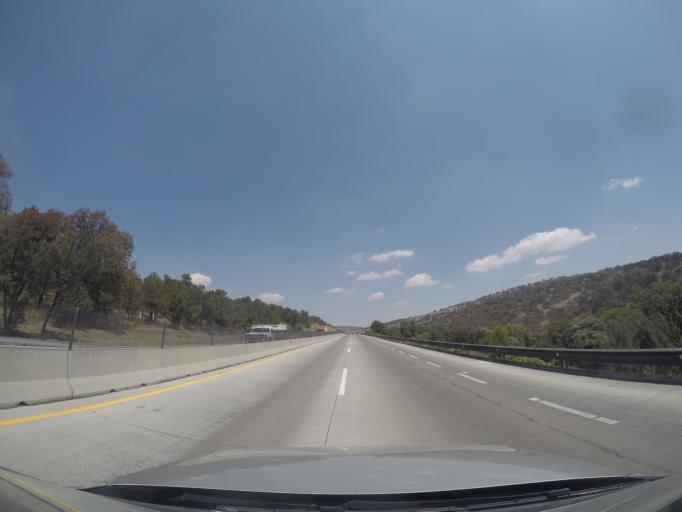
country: MX
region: Puebla
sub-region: San Matias Tlalancaleca
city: San Francisco Tlaloc
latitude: 19.3845
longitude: -98.4200
